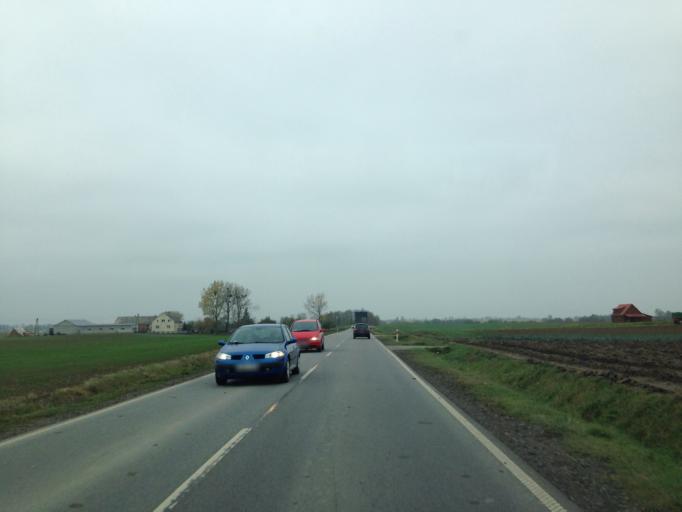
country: PL
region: Kujawsko-Pomorskie
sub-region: Powiat grudziadzki
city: Radzyn Chelminski
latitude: 53.4104
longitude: 18.9149
